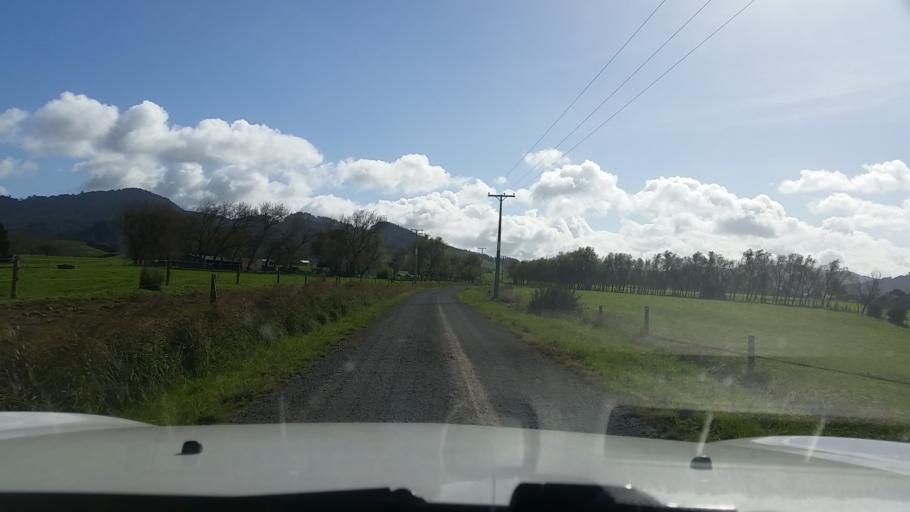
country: NZ
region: Waikato
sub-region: Hauraki District
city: Ngatea
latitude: -37.5066
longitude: 175.4069
